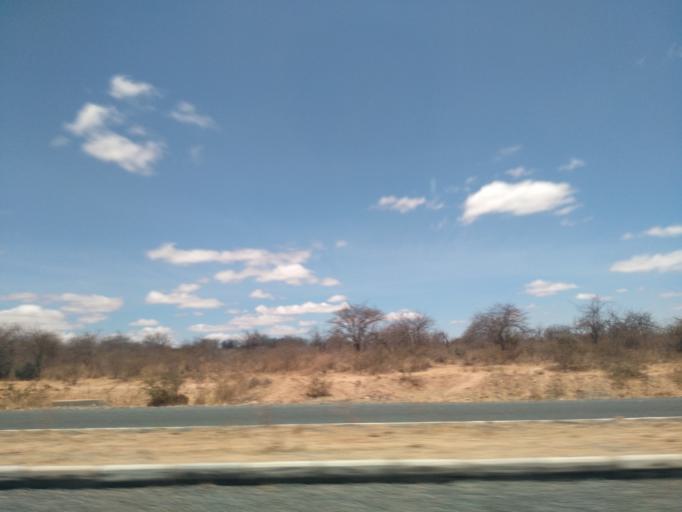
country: TZ
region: Dodoma
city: Kisasa
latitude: -6.1762
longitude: 35.8367
